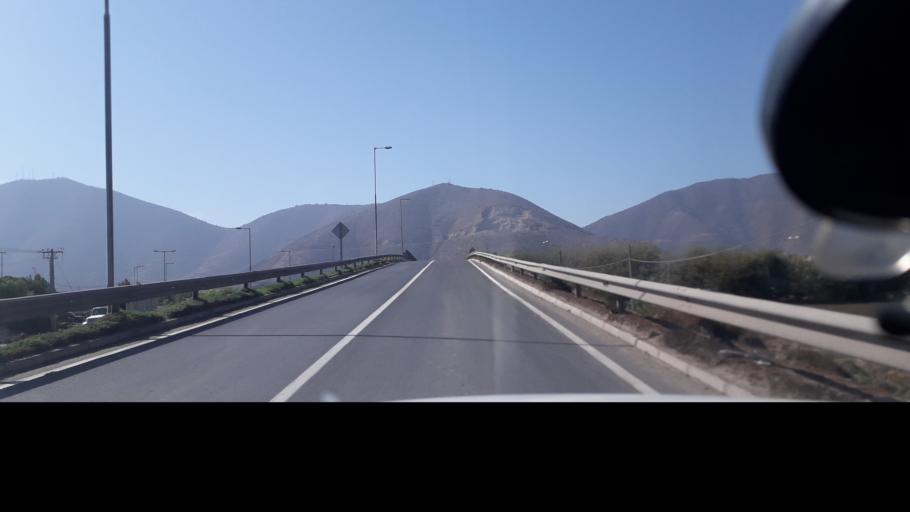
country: CL
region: Valparaiso
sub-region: Provincia de San Felipe
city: Llaillay
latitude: -32.8522
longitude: -70.9433
